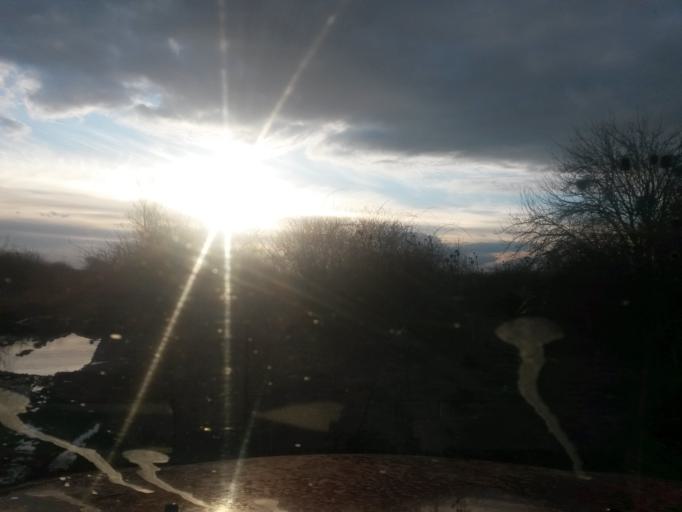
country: SK
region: Kosicky
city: Sobrance
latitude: 48.7017
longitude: 22.0728
